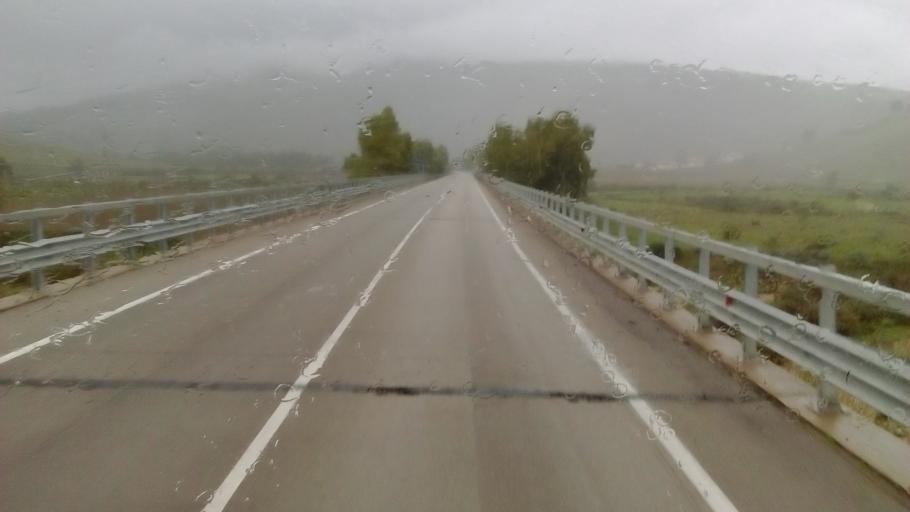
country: IT
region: Sicily
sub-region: Enna
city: Villarosa
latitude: 37.5309
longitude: 14.1296
